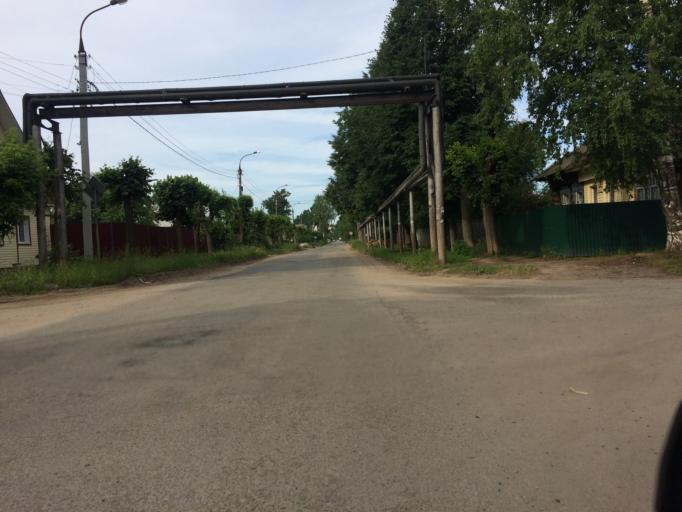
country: RU
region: Mariy-El
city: Yoshkar-Ola
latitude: 56.6508
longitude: 47.9136
